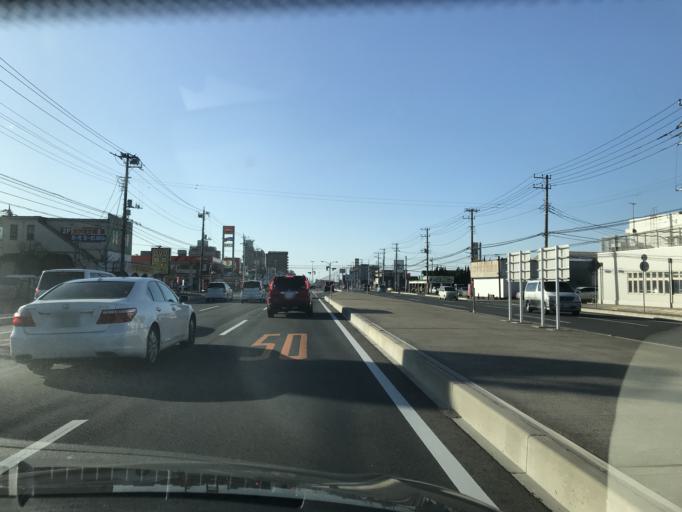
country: JP
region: Chiba
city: Omigawa
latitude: 35.8924
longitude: 140.6565
